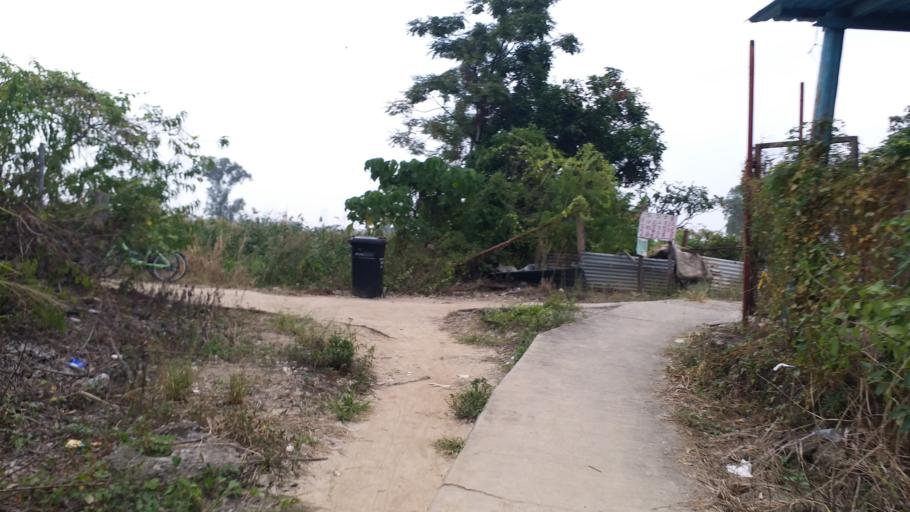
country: HK
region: Yuen Long
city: Yuen Long Kau Hui
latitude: 22.4553
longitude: 114.0354
